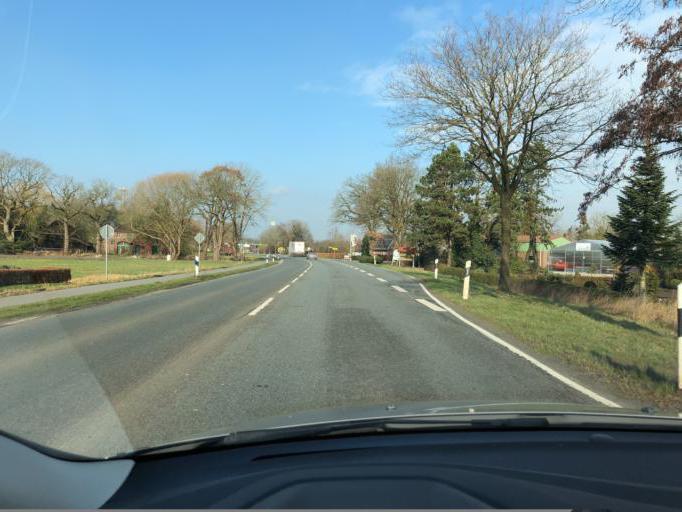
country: DE
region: Lower Saxony
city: Westerstede
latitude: 53.2846
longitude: 7.8976
